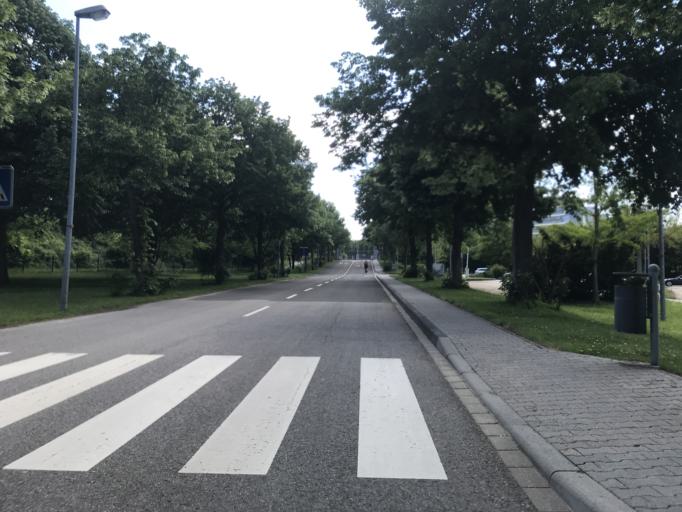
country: DE
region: Rheinland-Pfalz
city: Ingelheim am Rhein
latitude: 49.9760
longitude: 8.0509
